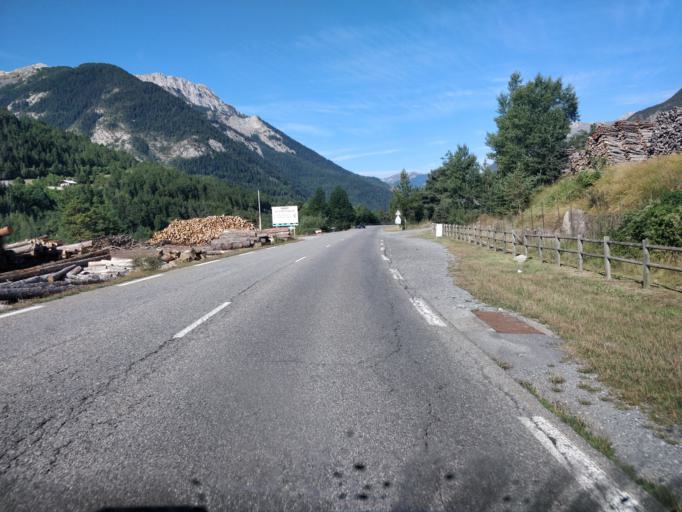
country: FR
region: Provence-Alpes-Cote d'Azur
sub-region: Departement des Alpes-de-Haute-Provence
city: Barcelonnette
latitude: 44.3899
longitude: 6.5840
